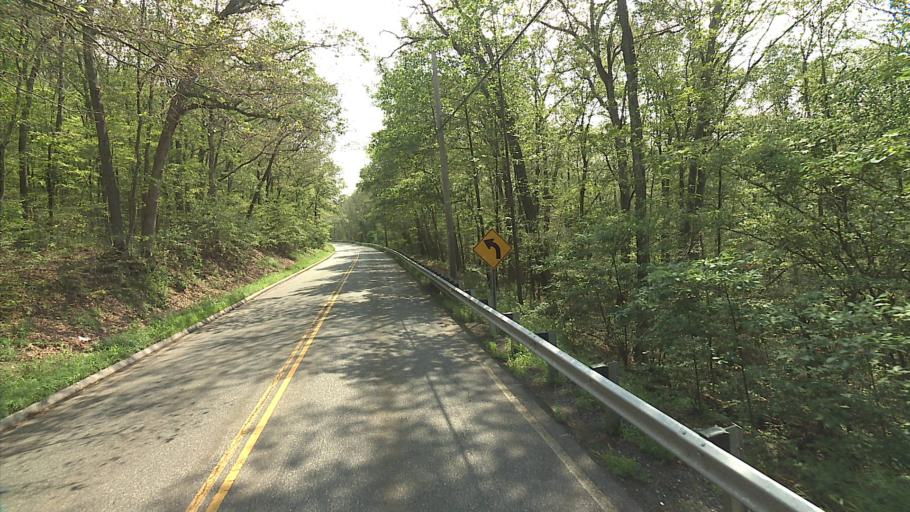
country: US
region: Connecticut
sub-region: New London County
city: Montville Center
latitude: 41.5008
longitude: -72.1713
